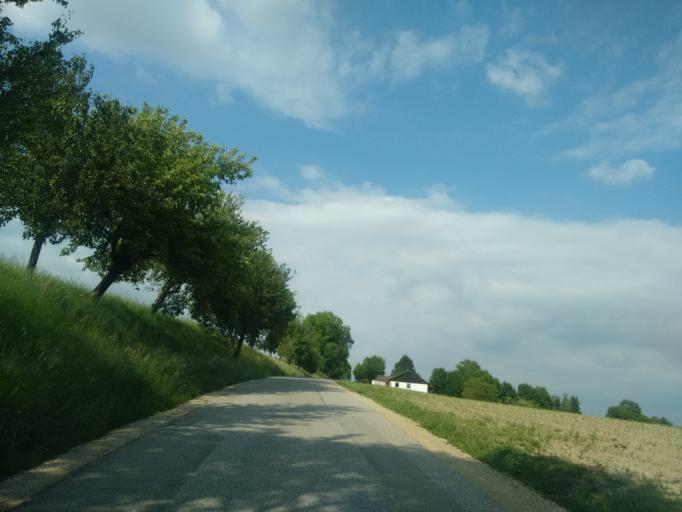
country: AT
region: Upper Austria
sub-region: Politischer Bezirk Grieskirchen
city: Bad Schallerbach
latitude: 48.1889
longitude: 13.8985
